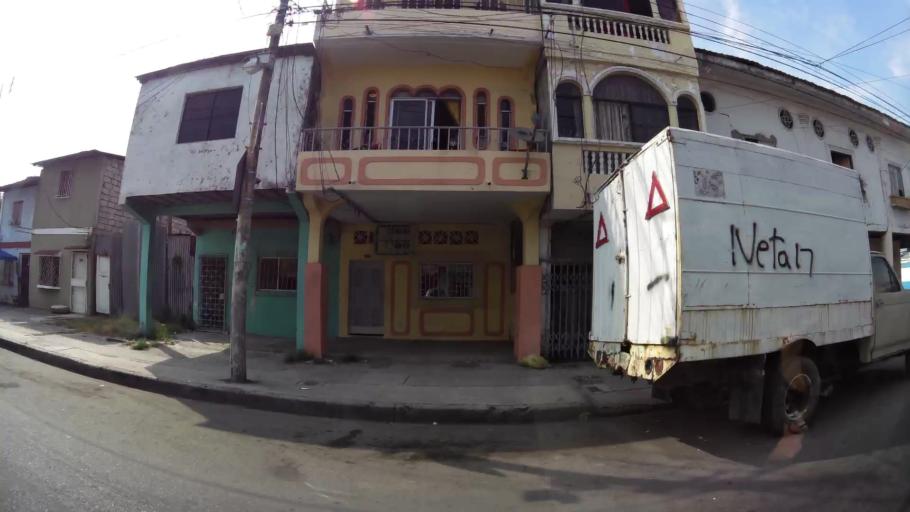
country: EC
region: Guayas
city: Guayaquil
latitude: -2.2171
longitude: -79.9056
